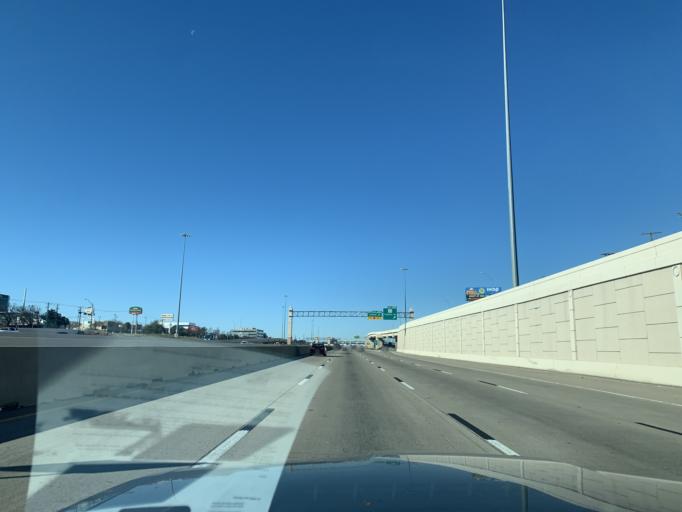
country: US
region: Texas
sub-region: Tarrant County
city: Arlington
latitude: 32.7600
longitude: -97.0867
